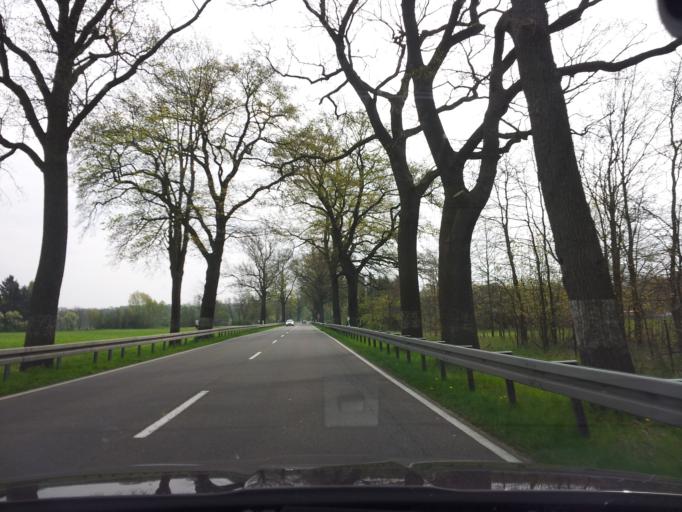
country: DE
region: Brandenburg
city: Rehfelde
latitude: 52.4801
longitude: 13.9571
